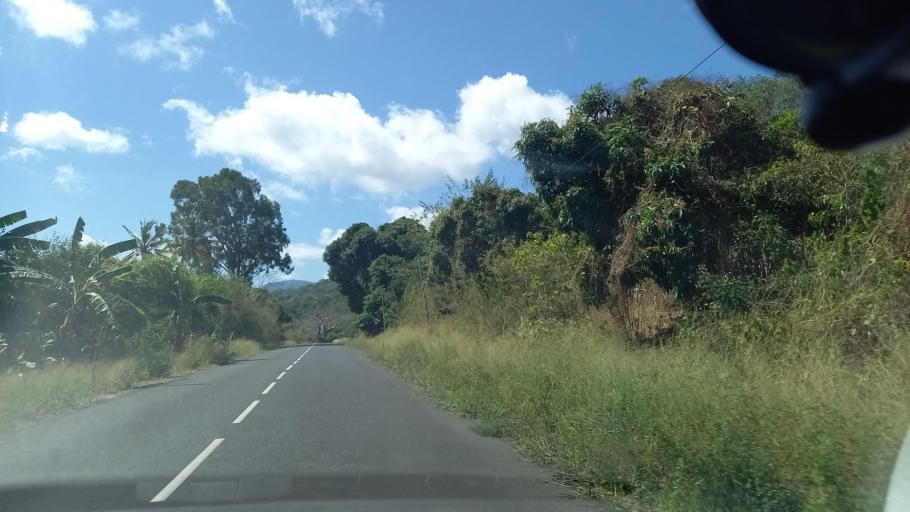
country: YT
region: Kani-Keli
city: Kani Keli
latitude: -12.9492
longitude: 45.0989
